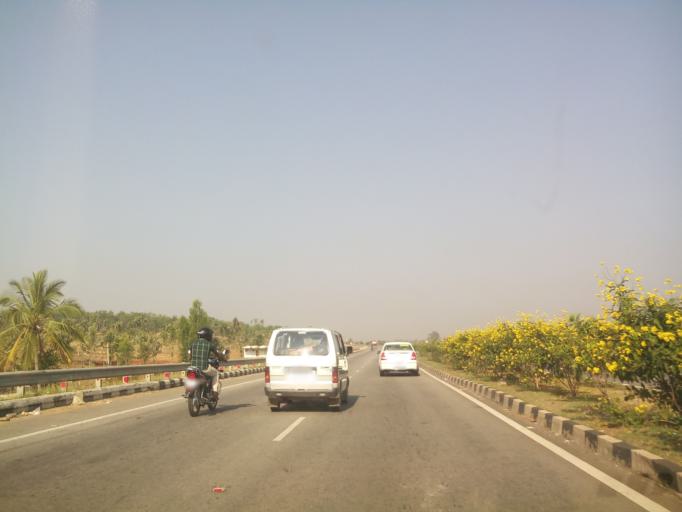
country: IN
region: Karnataka
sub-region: Bangalore Rural
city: Nelamangala
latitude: 13.0659
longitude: 77.3133
